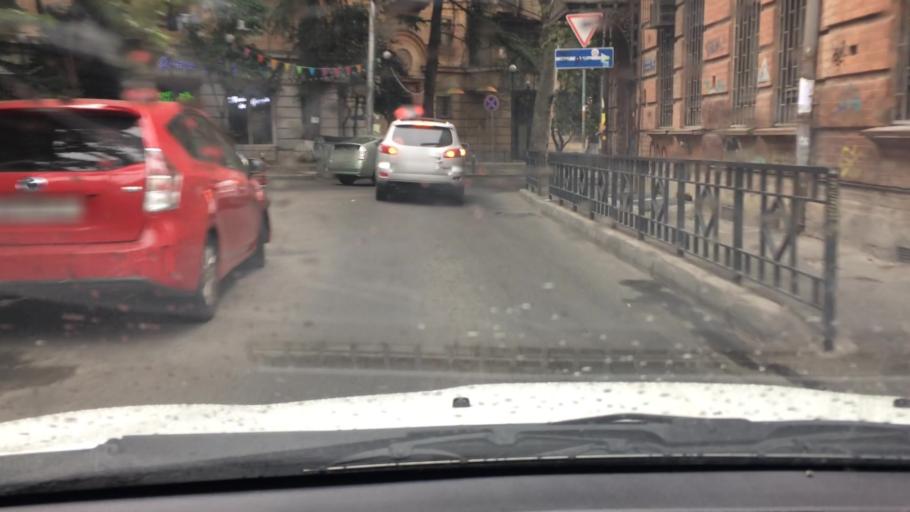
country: GE
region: T'bilisi
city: Tbilisi
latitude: 41.7092
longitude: 44.8032
